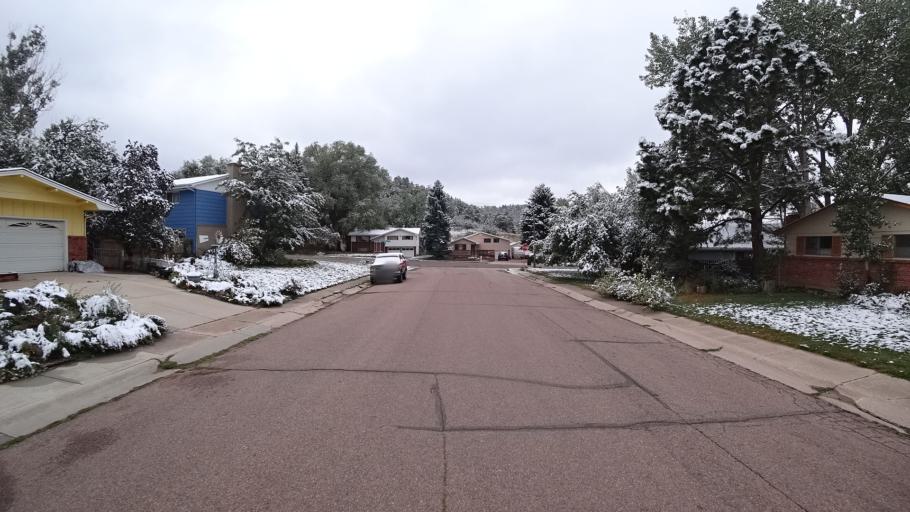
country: US
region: Colorado
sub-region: El Paso County
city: Colorado Springs
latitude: 38.8906
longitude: -104.7811
